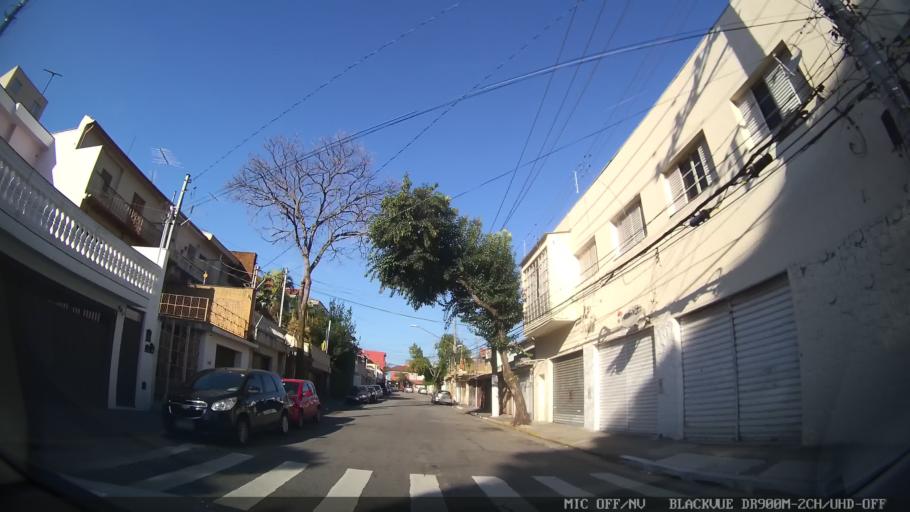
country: BR
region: Sao Paulo
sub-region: Sao Paulo
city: Sao Paulo
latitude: -23.4998
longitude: -46.6173
